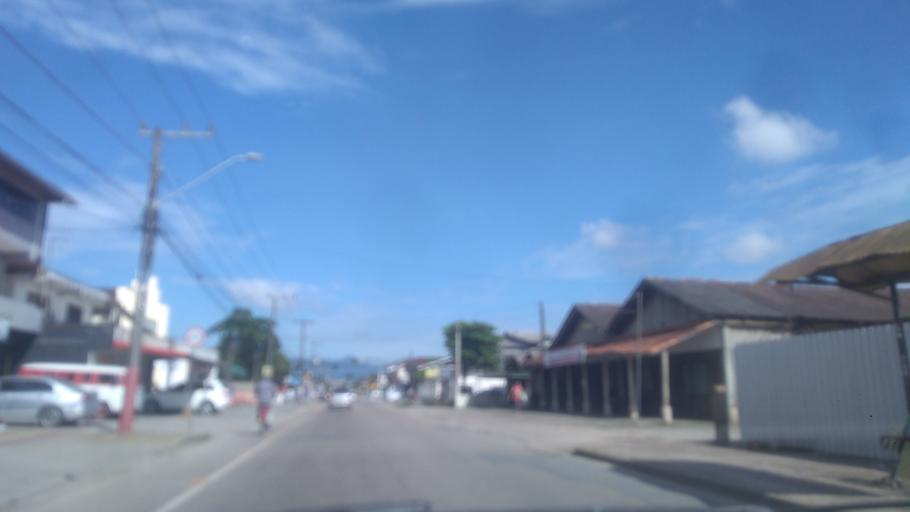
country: BR
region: Santa Catarina
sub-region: Joinville
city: Joinville
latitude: -26.3206
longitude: -48.8151
